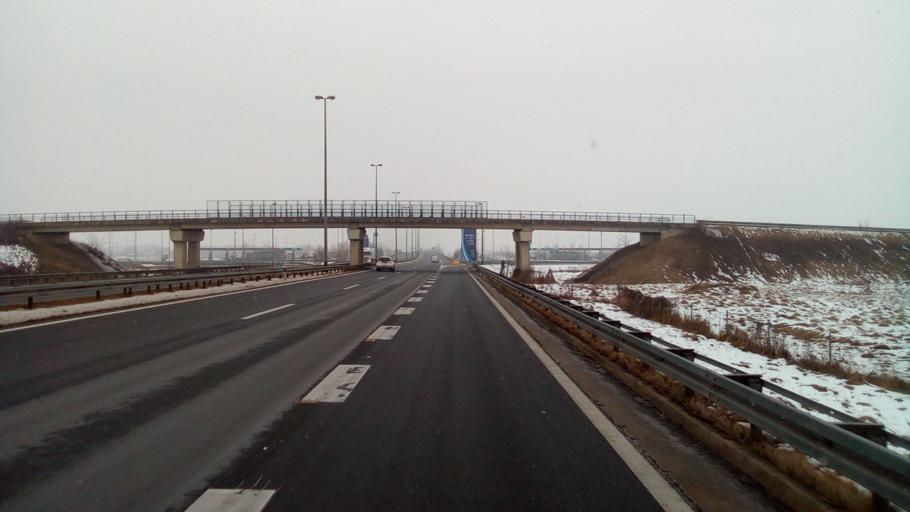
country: HR
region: Zagrebacka
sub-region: Grad Samobor
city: Samobor
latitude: 45.8245
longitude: 15.7428
